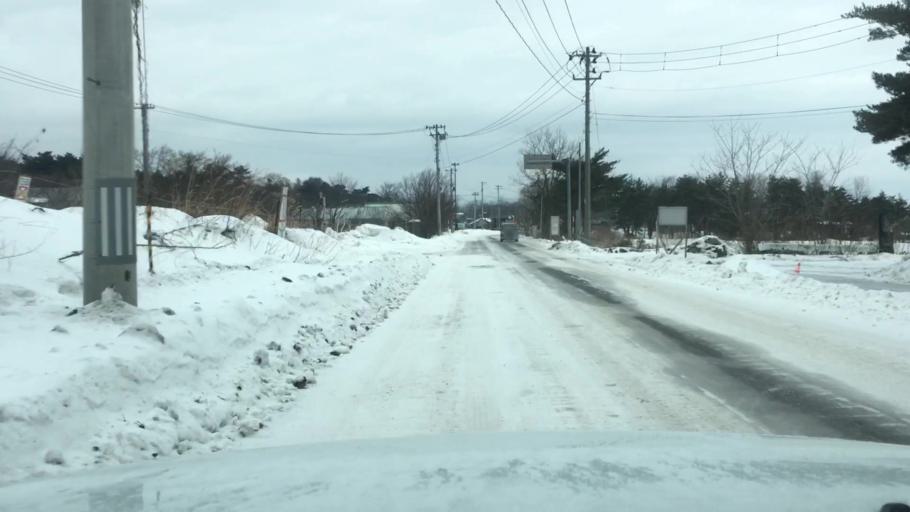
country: JP
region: Iwate
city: Shizukuishi
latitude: 39.9132
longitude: 141.0051
